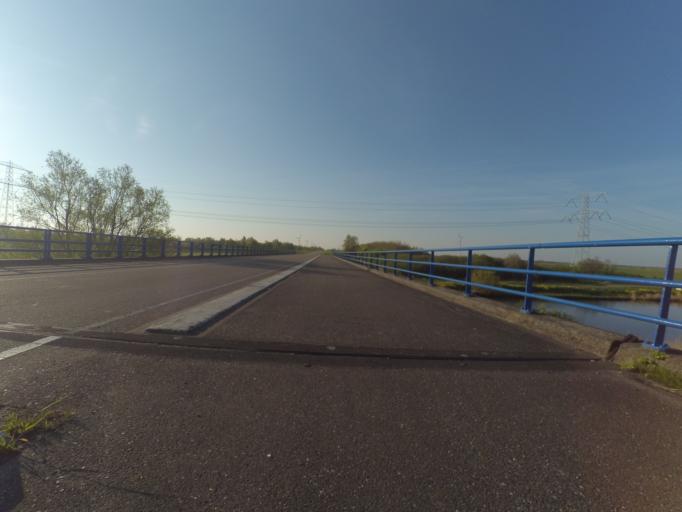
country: NL
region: Flevoland
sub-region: Gemeente Lelystad
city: Lelystad
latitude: 52.4272
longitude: 5.3964
